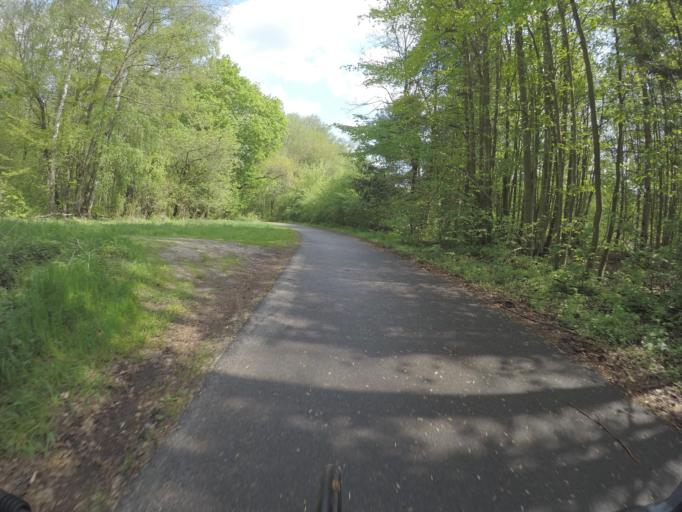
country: DE
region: Brandenburg
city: Marienwerder
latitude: 52.8548
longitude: 13.6116
